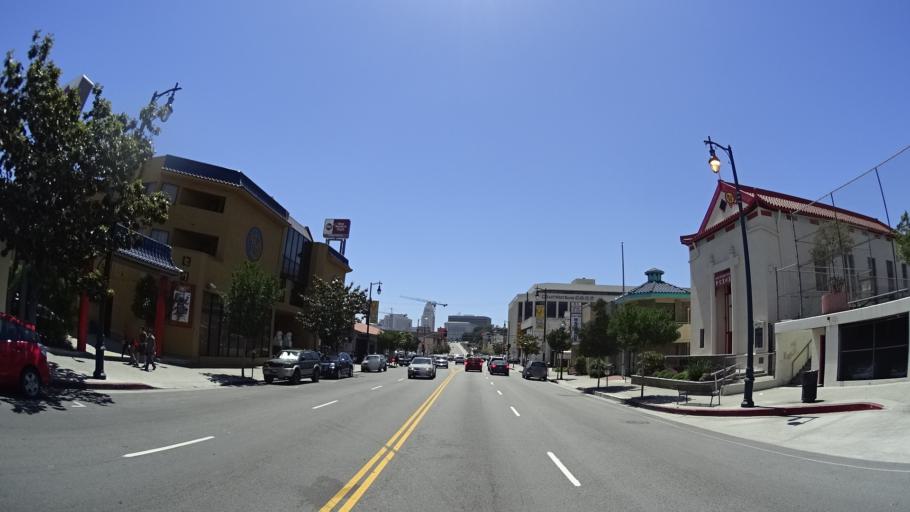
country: US
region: California
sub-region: Los Angeles County
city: Los Angeles
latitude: 34.0635
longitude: -118.2392
